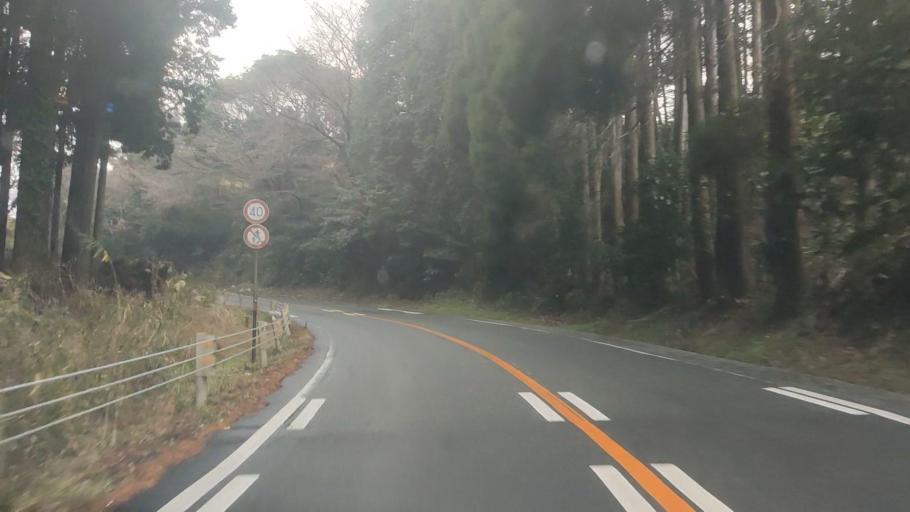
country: JP
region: Kumamoto
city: Aso
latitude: 32.8967
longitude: 130.9987
